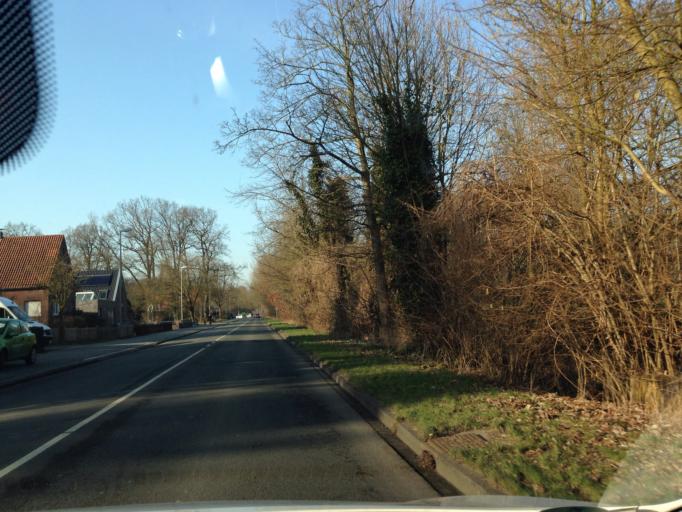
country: DE
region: North Rhine-Westphalia
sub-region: Regierungsbezirk Munster
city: Muenster
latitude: 51.9994
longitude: 7.6173
